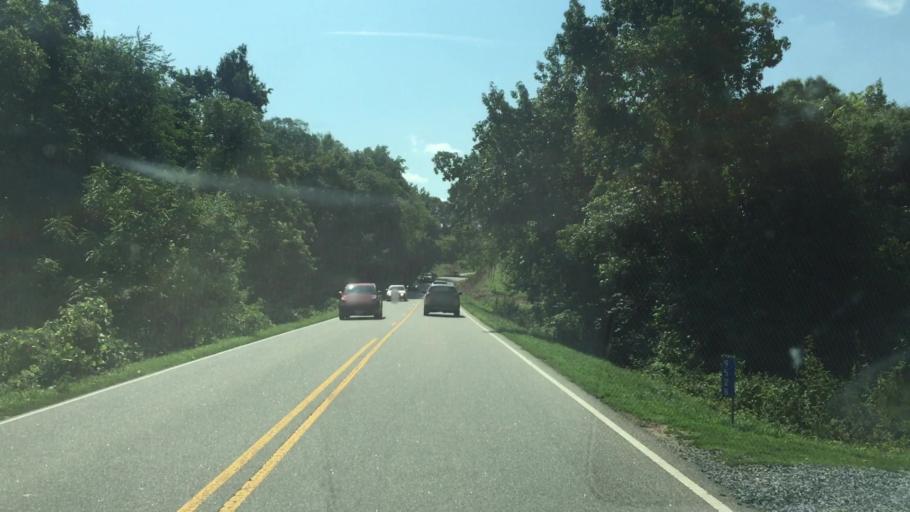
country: US
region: North Carolina
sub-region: Anson County
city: Burnsville
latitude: 35.0913
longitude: -80.2985
